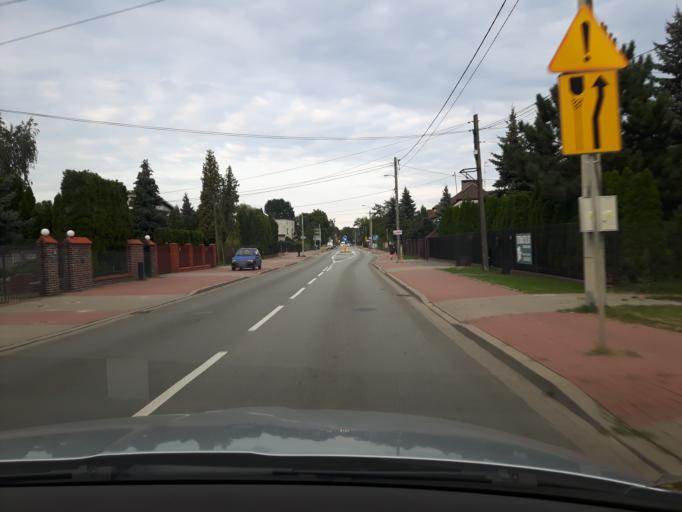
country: PL
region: Masovian Voivodeship
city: Zielonka
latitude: 52.3114
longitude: 21.1428
